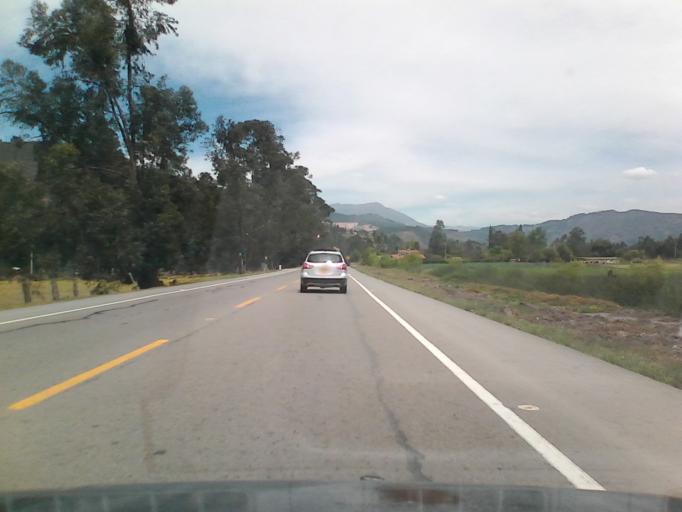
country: CO
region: Boyaca
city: Tibasosa
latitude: 5.7766
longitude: -72.9965
